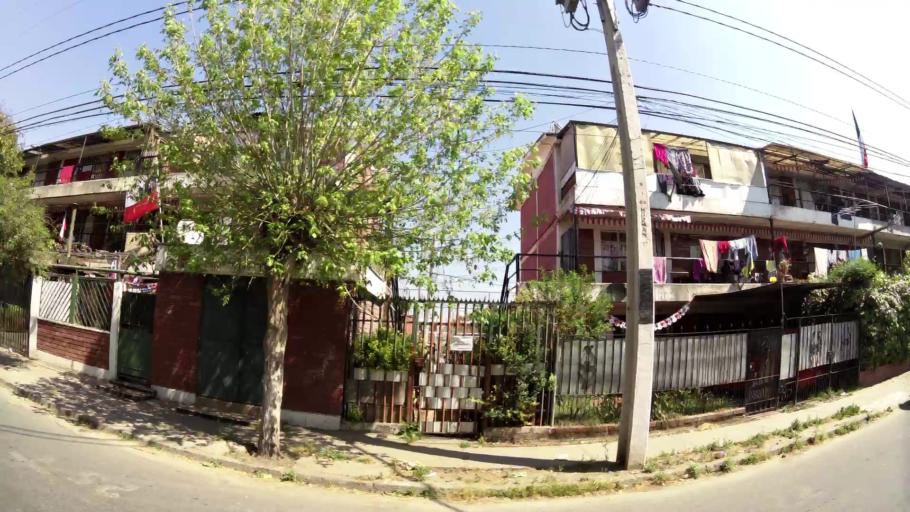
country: CL
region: Santiago Metropolitan
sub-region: Provincia de Santiago
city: La Pintana
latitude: -33.5565
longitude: -70.6053
